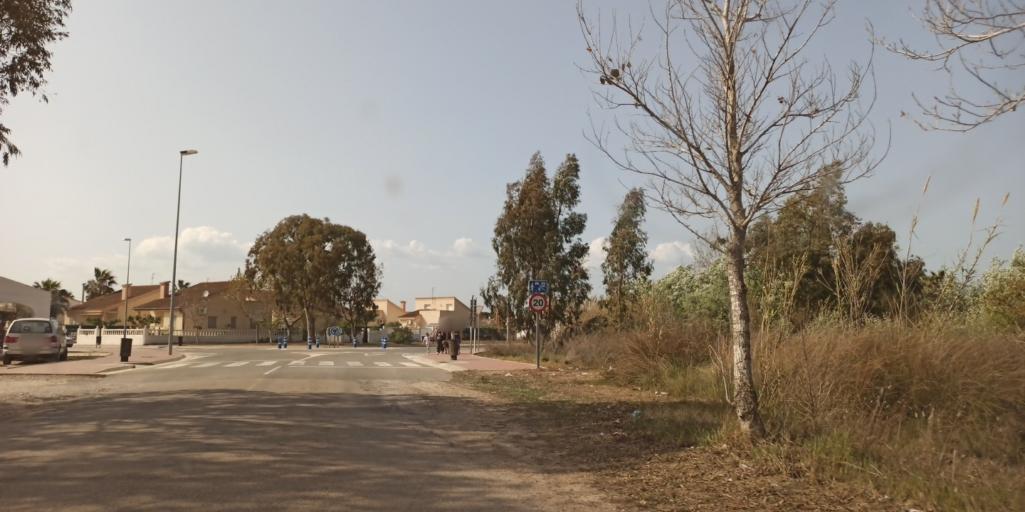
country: ES
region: Catalonia
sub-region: Provincia de Tarragona
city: Deltebre
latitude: 40.7231
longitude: 0.8432
